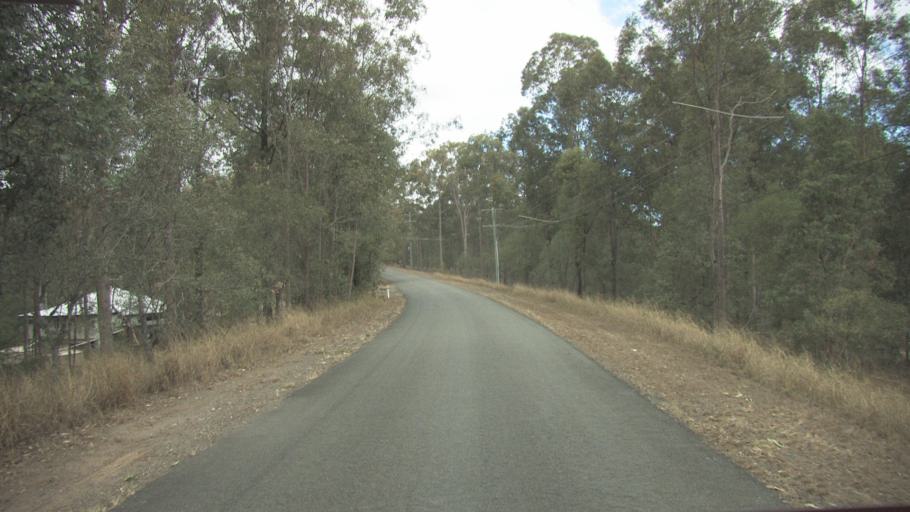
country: AU
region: Queensland
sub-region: Logan
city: Cedar Vale
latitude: -27.8938
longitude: 153.0248
